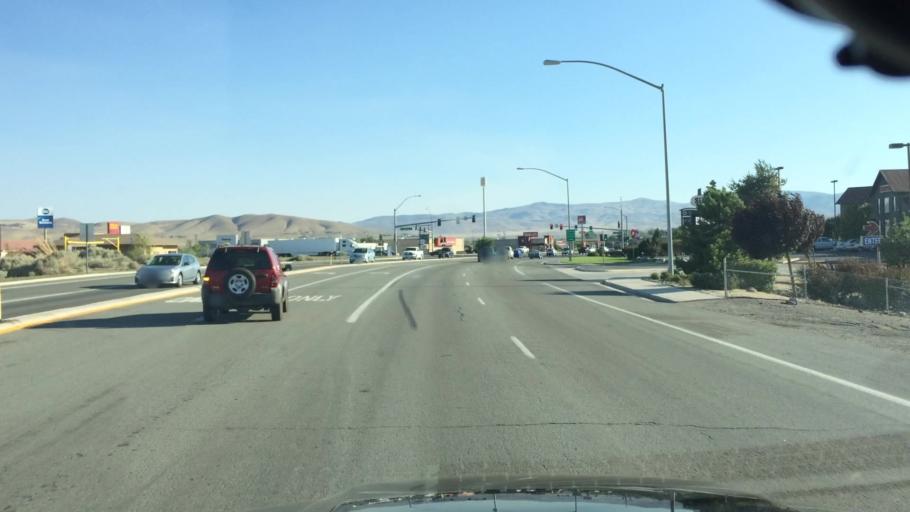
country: US
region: Nevada
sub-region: Lyon County
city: Fernley
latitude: 39.6110
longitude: -119.2190
